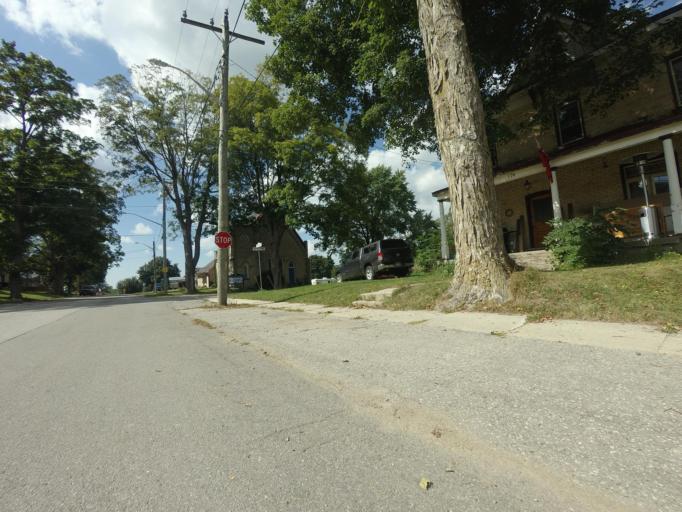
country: CA
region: Ontario
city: Huron East
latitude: 43.7370
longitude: -81.4308
